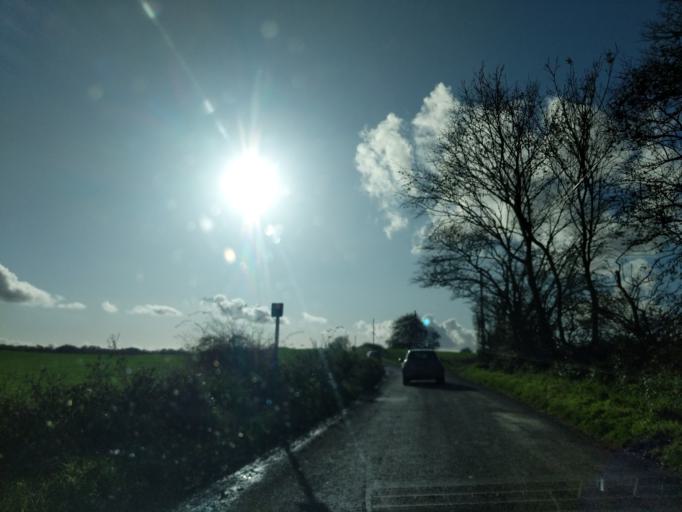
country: GB
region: Scotland
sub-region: Dumfries and Galloway
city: Dalbeattie
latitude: 54.9921
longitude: -3.8395
